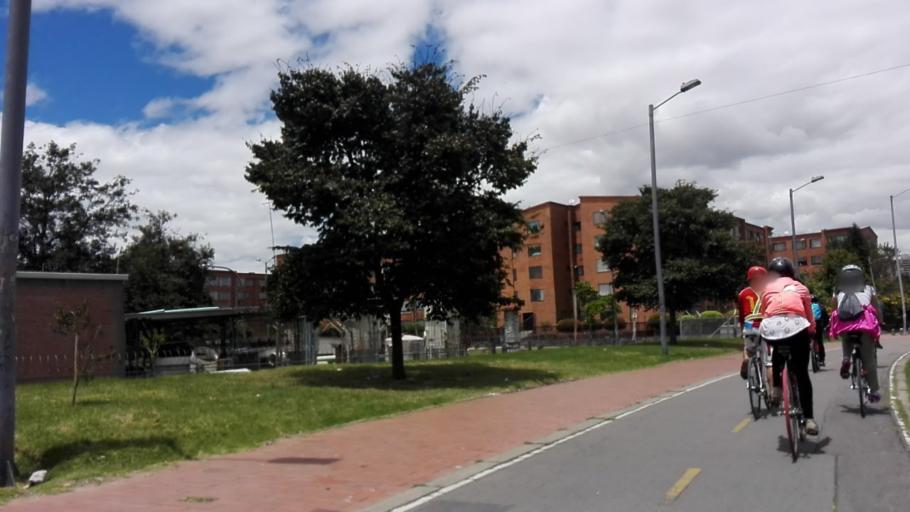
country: CO
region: Bogota D.C.
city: Barrio San Luis
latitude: 4.6872
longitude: -74.0791
